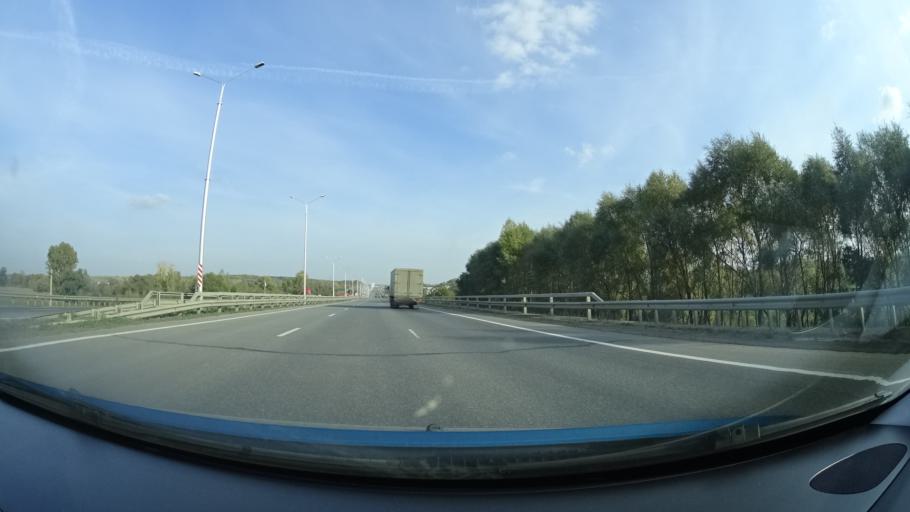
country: RU
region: Bashkortostan
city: Avdon
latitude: 54.6462
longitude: 55.5449
